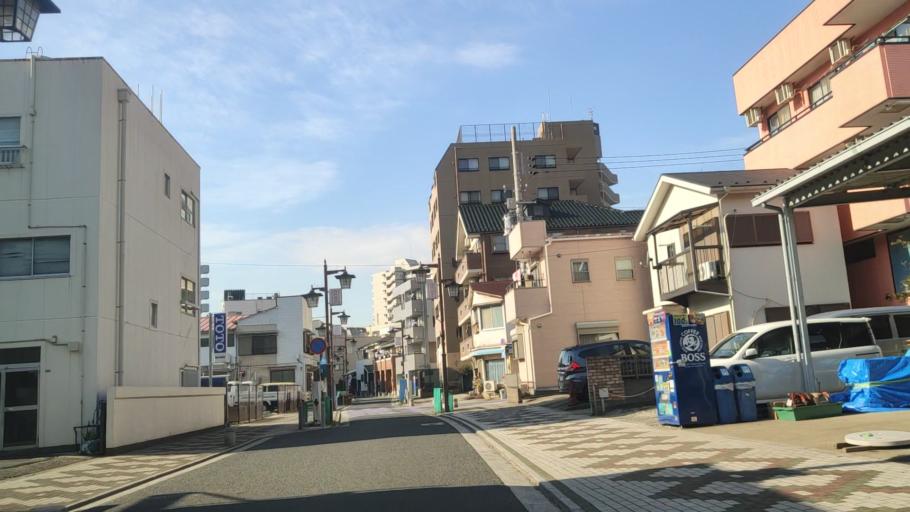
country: JP
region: Kanagawa
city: Yokohama
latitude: 35.4508
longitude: 139.6075
